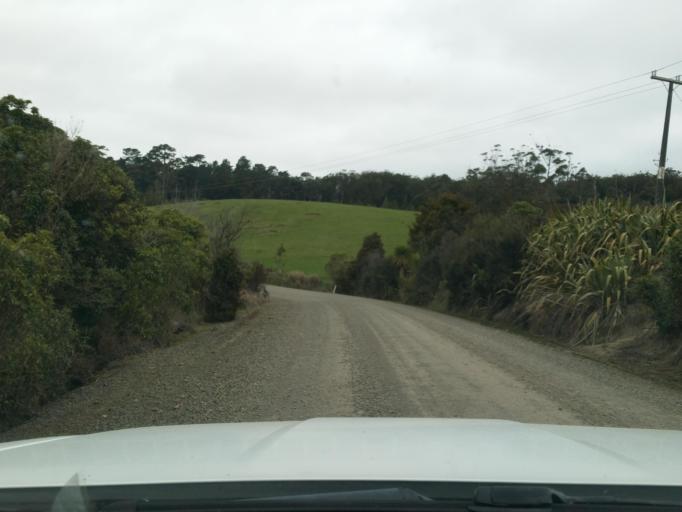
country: NZ
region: Northland
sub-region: Kaipara District
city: Dargaville
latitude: -35.7184
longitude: 173.6409
